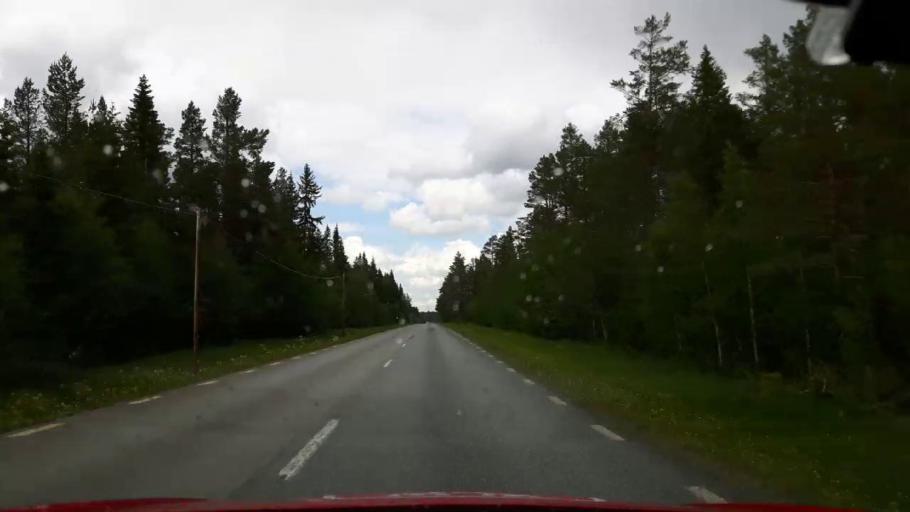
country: SE
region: Jaemtland
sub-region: Krokoms Kommun
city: Krokom
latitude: 63.5037
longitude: 14.2158
